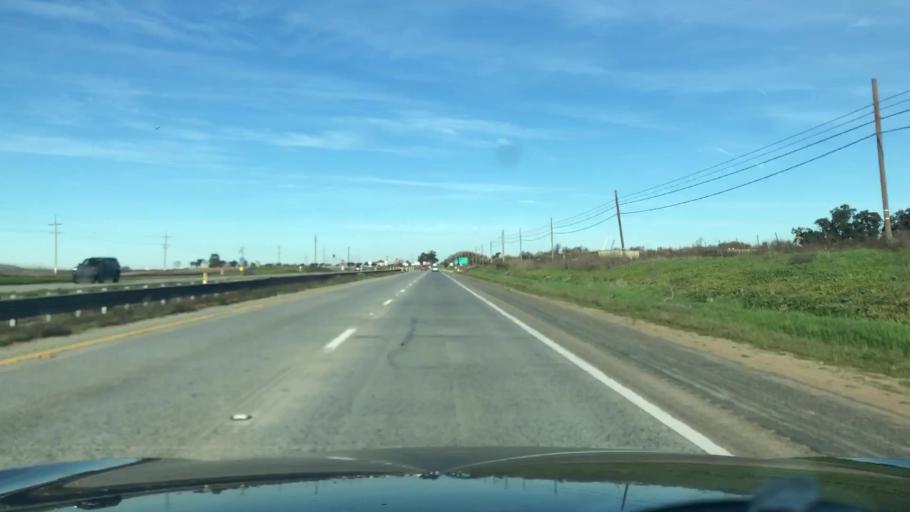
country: US
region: California
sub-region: Monterey County
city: Chualar
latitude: 36.5572
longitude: -121.5057
